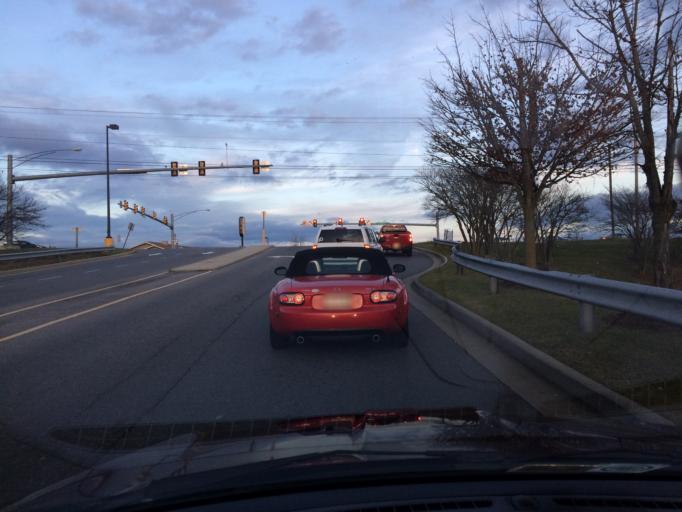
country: US
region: Virginia
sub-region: Montgomery County
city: Merrimac
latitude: 37.1614
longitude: -80.4235
